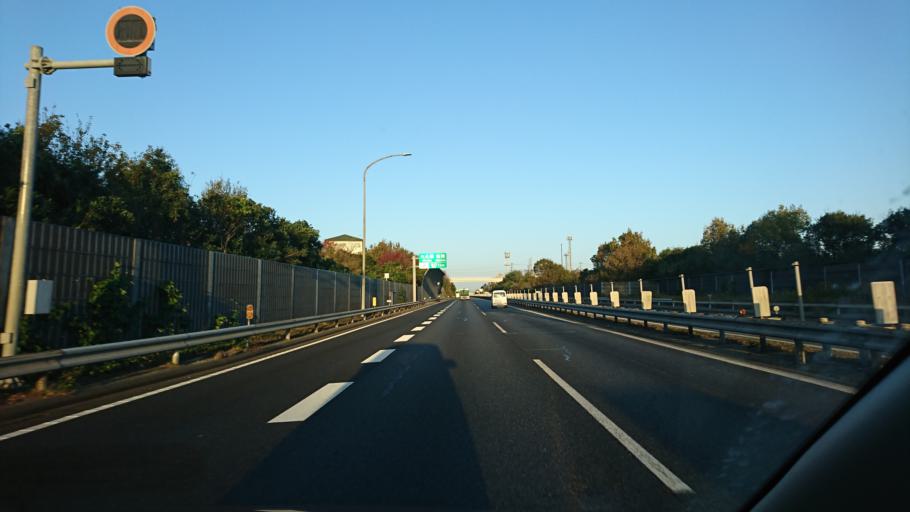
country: JP
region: Hyogo
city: Akashi
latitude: 34.7046
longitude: 134.9550
